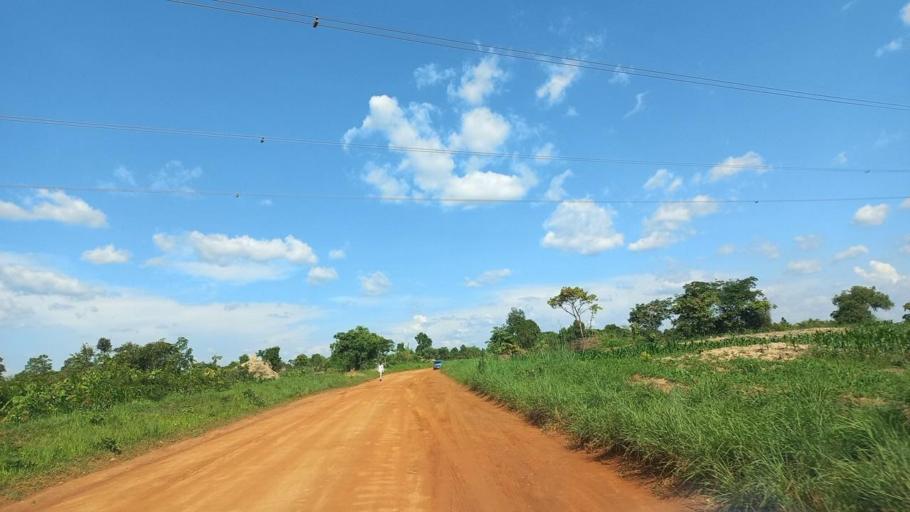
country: ZM
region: Copperbelt
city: Kitwe
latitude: -12.8706
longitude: 28.3459
